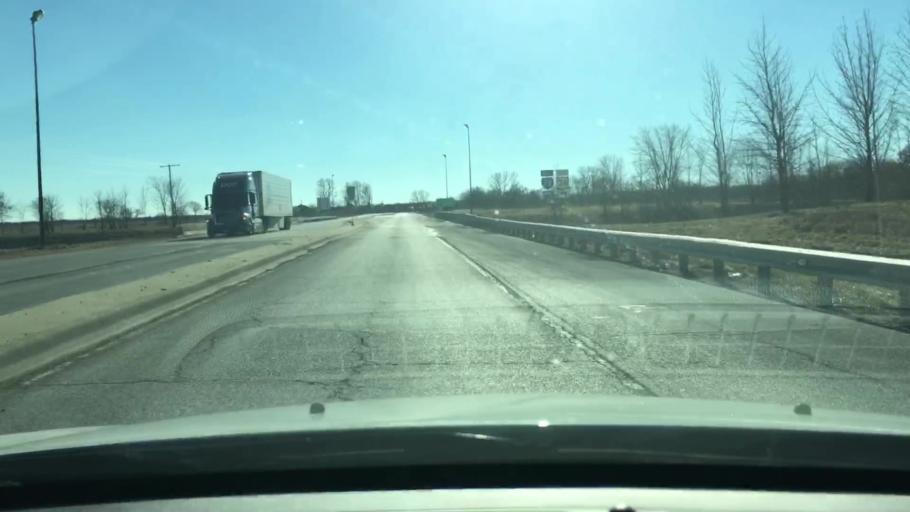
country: US
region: Illinois
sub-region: Pike County
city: Griggsville
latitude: 39.6749
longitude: -90.7685
